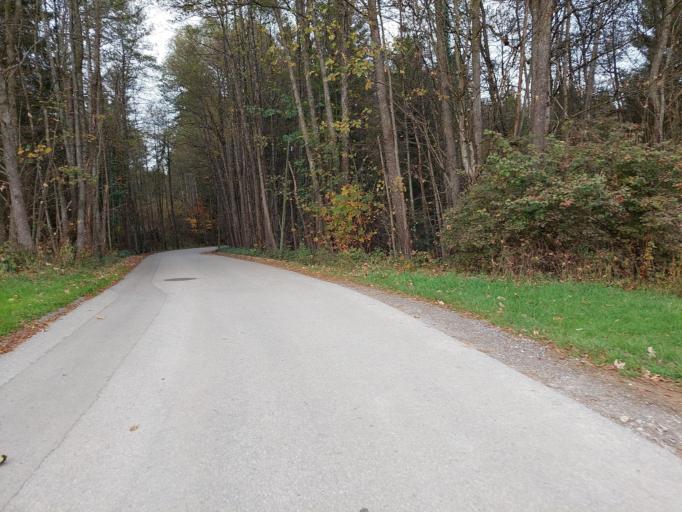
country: AT
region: Tyrol
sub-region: Politischer Bezirk Kufstein
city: Angath
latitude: 47.4975
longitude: 12.0505
